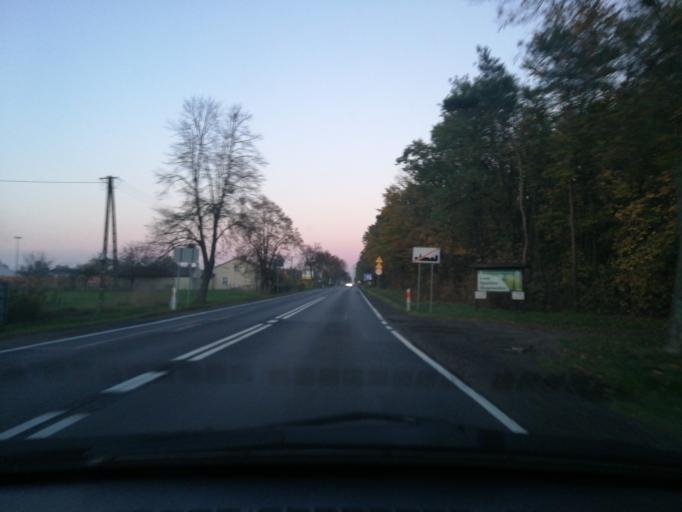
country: PL
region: Lodz Voivodeship
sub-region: Powiat lodzki wschodni
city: Andrespol
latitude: 51.7985
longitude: 19.6363
